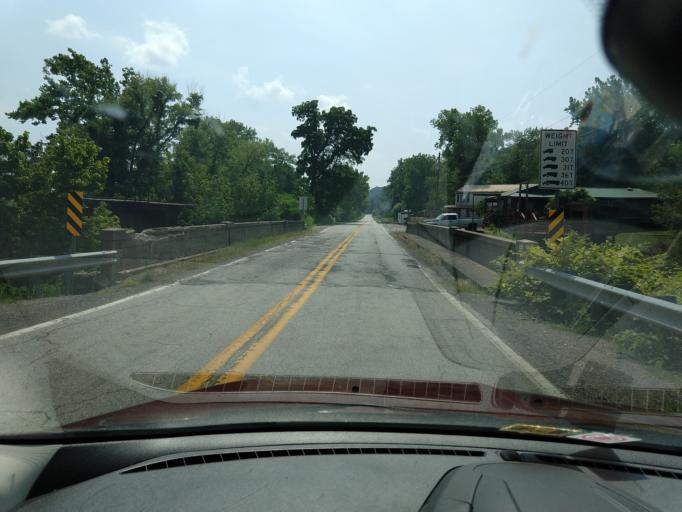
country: US
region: West Virginia
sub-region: Mason County
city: New Haven
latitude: 38.8747
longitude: -81.9115
